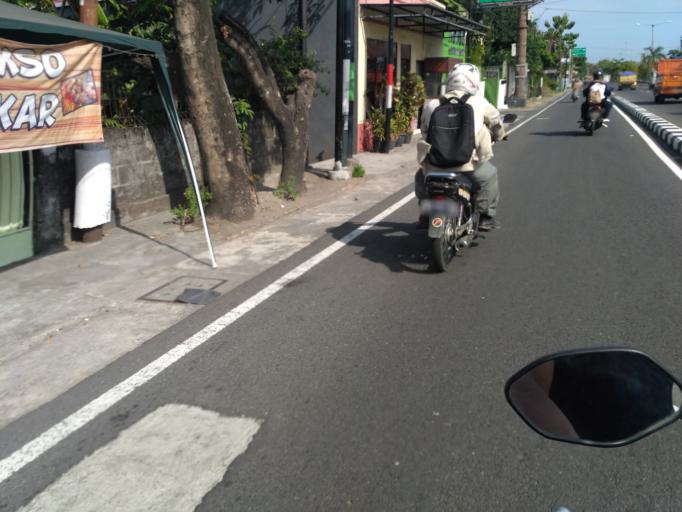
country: ID
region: Daerah Istimewa Yogyakarta
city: Depok
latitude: -7.7796
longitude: 110.4302
